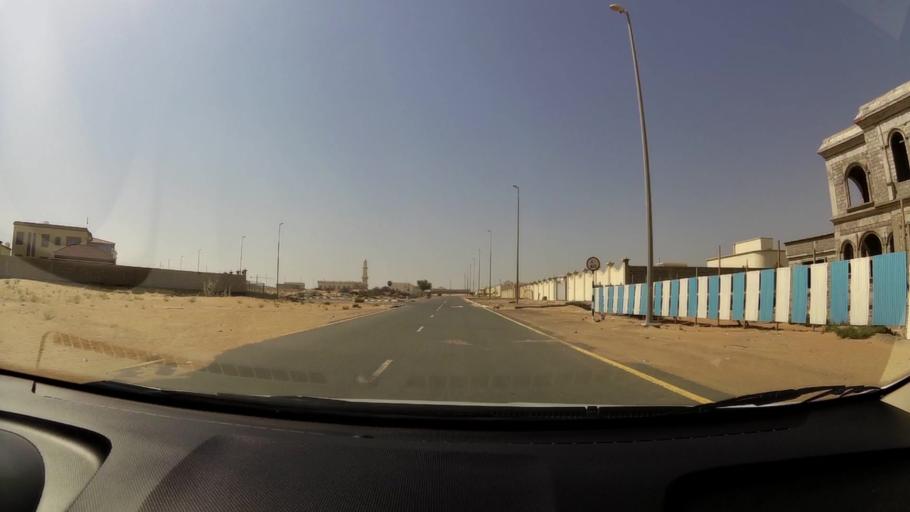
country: AE
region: Umm al Qaywayn
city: Umm al Qaywayn
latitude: 25.4899
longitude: 55.6107
